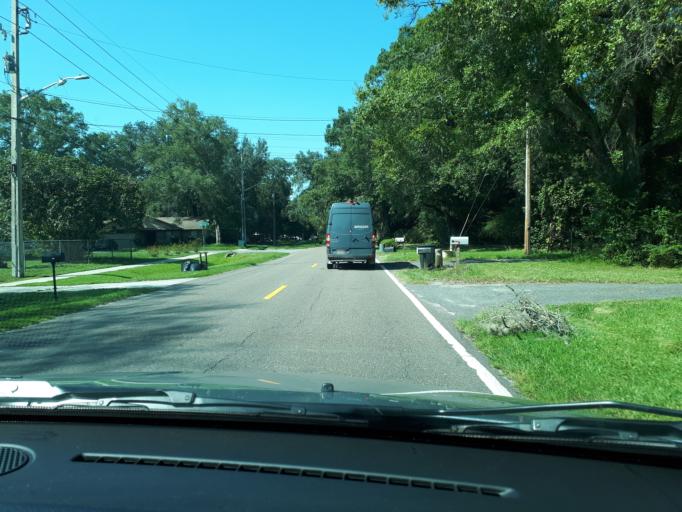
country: US
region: Florida
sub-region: Clay County
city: Bellair-Meadowbrook Terrace
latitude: 30.2792
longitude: -81.8317
